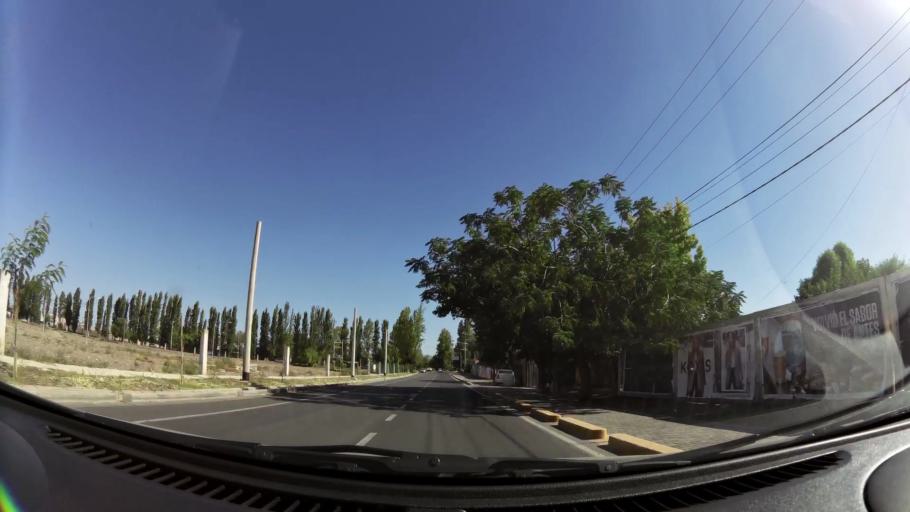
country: AR
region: Mendoza
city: Villa Nueva
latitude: -32.9194
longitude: -68.8004
